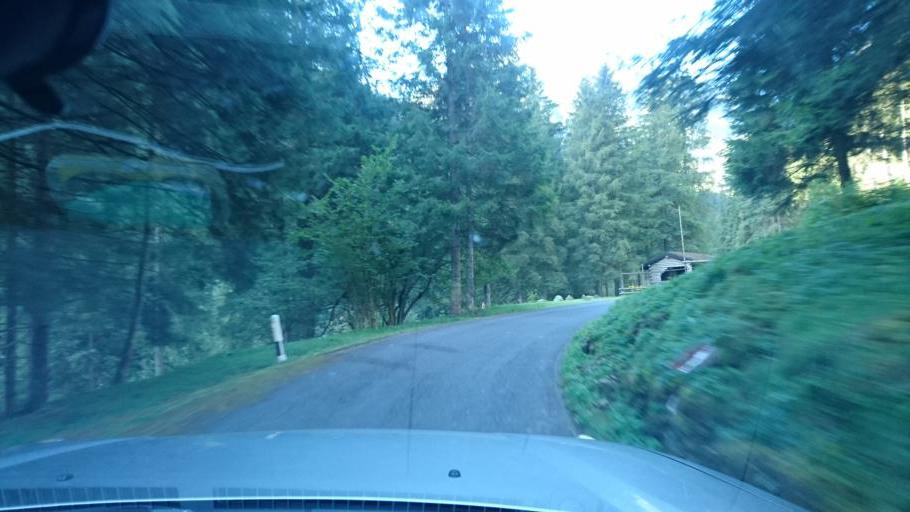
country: IT
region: Lombardy
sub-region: Provincia di Brescia
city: Paisco Loveno
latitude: 46.0533
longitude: 10.2392
